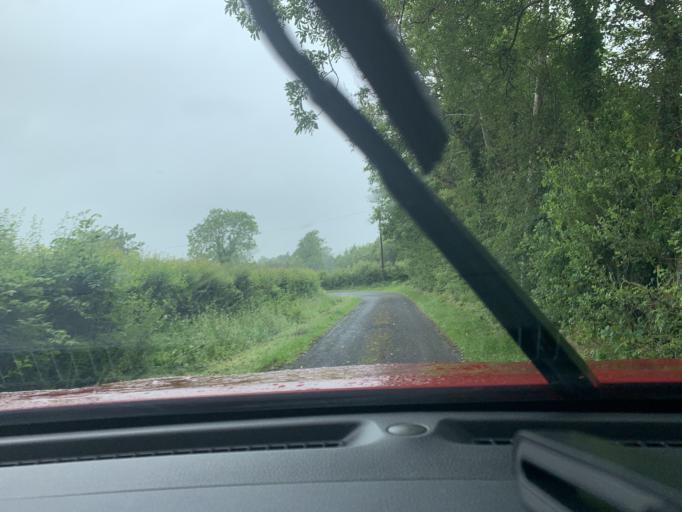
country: GB
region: Northern Ireland
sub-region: Fermanagh District
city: Enniskillen
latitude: 54.2660
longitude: -7.7401
